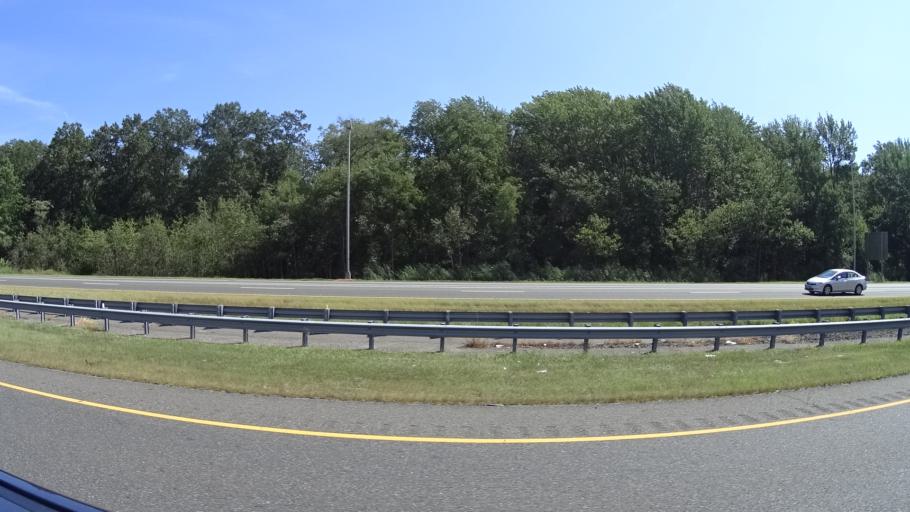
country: US
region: New Jersey
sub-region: Monmouth County
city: Eatontown
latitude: 40.2635
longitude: -74.0598
